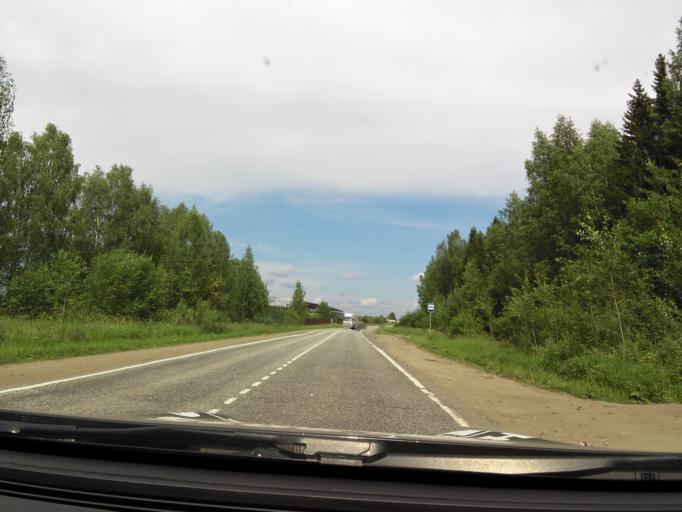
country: RU
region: Kirov
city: Vakhrushi
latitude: 58.6653
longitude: 49.9291
